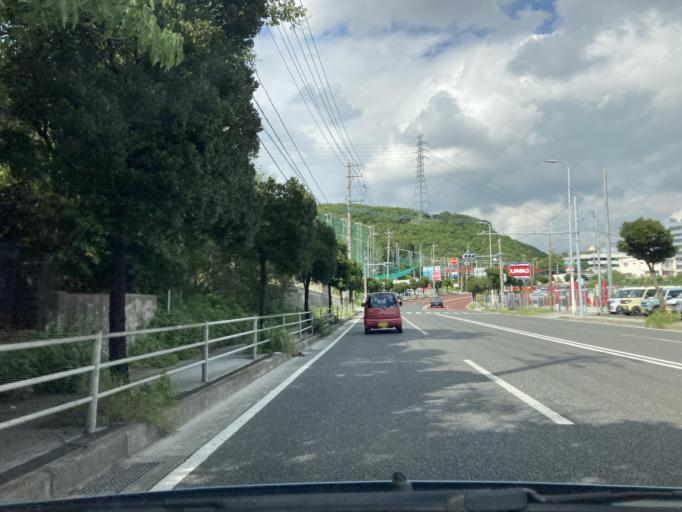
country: JP
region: Okinawa
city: Ginowan
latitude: 26.2347
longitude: 127.7696
